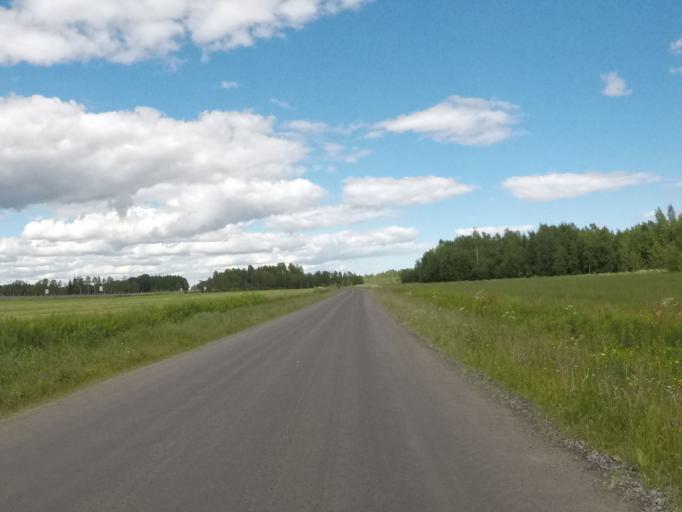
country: SE
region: Vaesterbotten
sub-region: Robertsfors Kommun
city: Robertsfors
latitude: 64.0785
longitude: 20.8670
